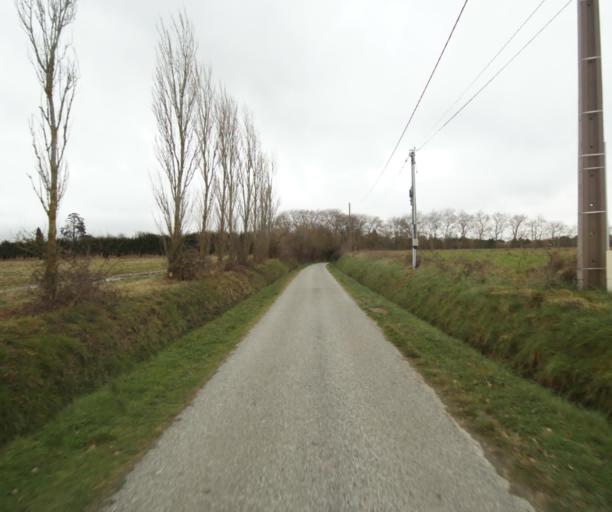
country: FR
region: Midi-Pyrenees
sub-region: Departement de l'Ariege
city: Mazeres
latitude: 43.2505
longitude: 1.6667
